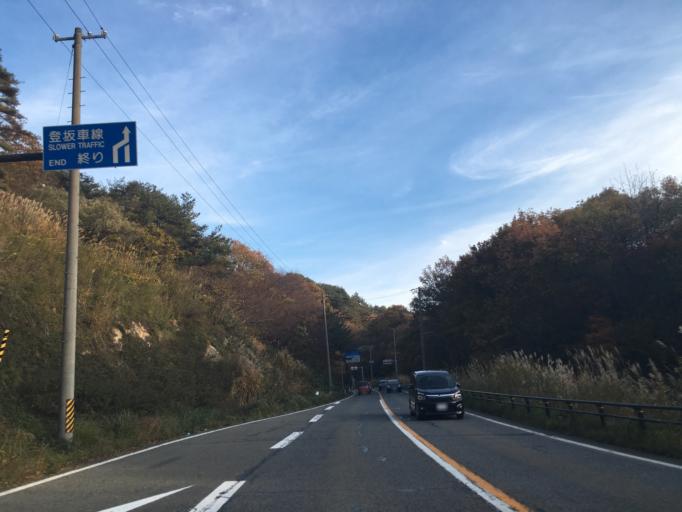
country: JP
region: Fukushima
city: Kitakata
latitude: 37.5690
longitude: 139.7150
